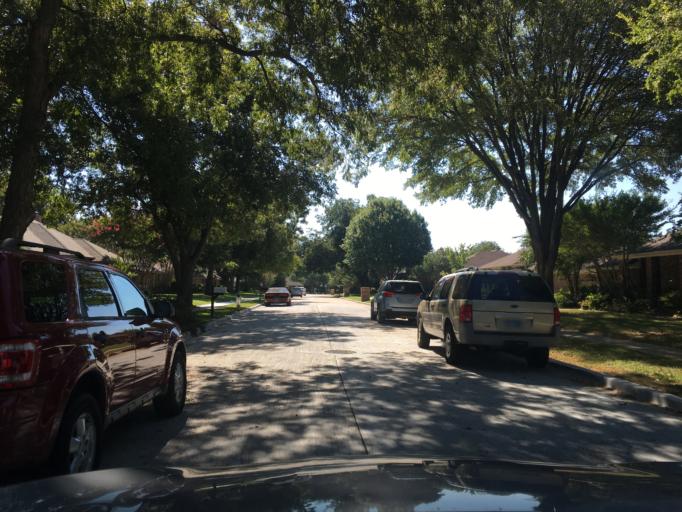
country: US
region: Texas
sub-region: Dallas County
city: Sachse
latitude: 32.9702
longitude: -96.6103
